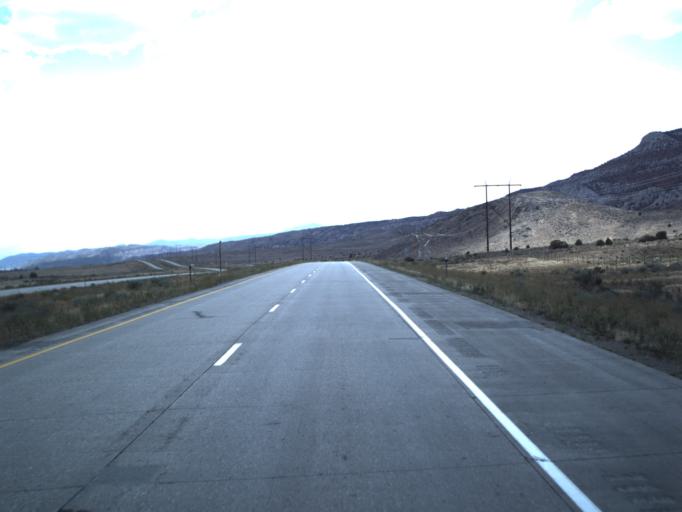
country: US
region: Utah
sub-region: Sevier County
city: Richfield
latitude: 38.8405
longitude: -112.0223
